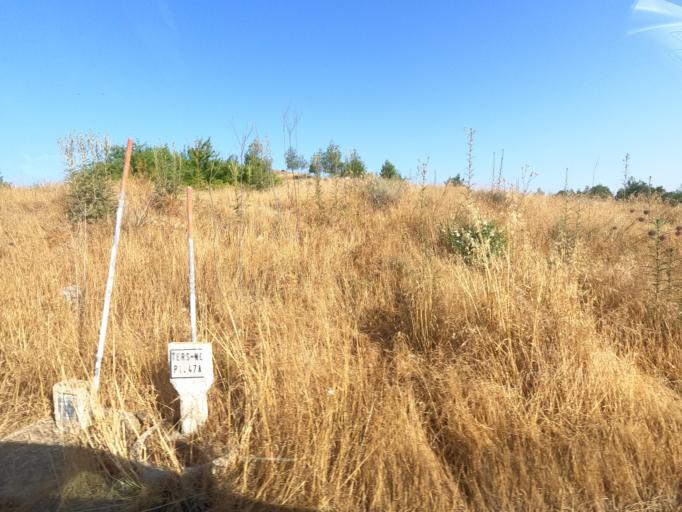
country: CY
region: Lefkosia
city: Lympia
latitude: 34.9895
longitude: 33.4370
